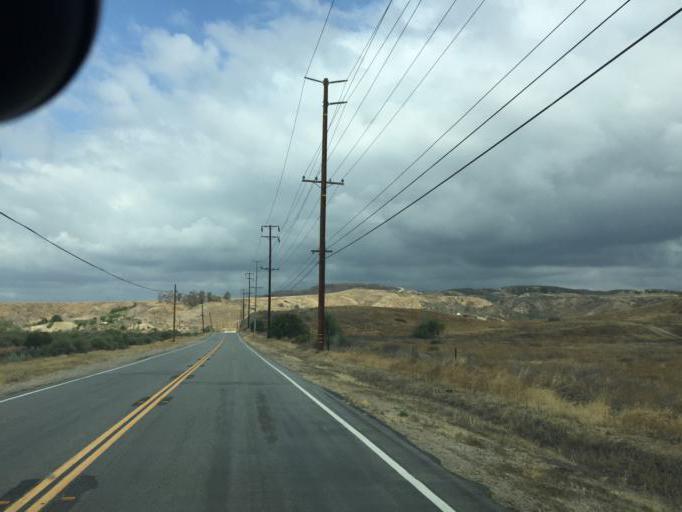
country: US
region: California
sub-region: Los Angeles County
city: Santa Clarita
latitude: 34.4739
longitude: -118.4598
